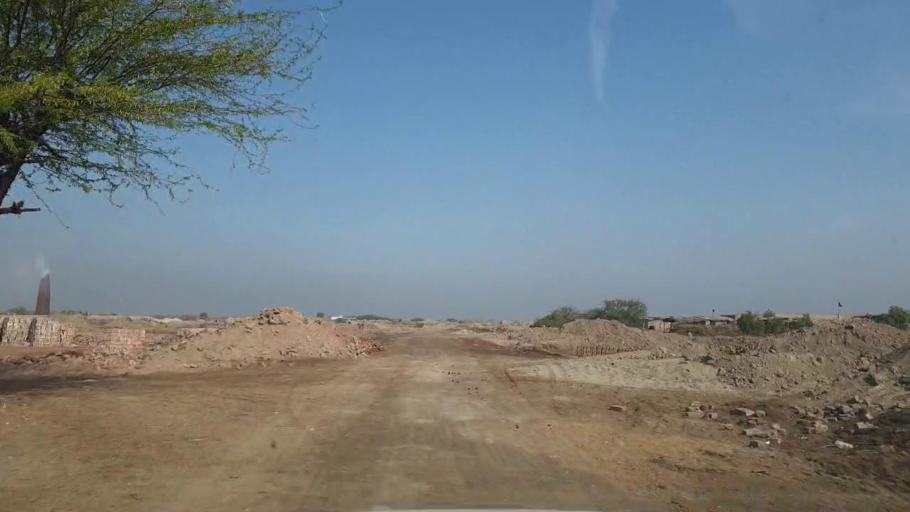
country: PK
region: Sindh
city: Mirpur Khas
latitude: 25.5180
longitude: 69.0681
